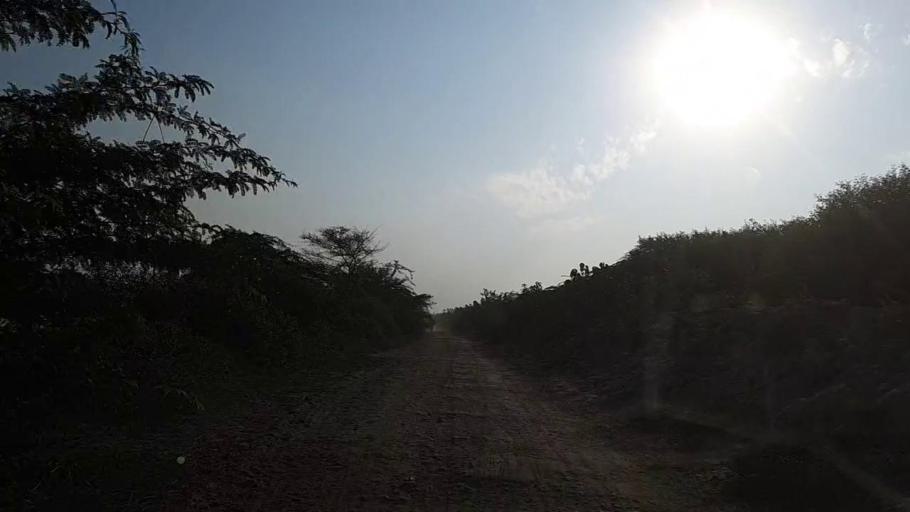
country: PK
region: Sindh
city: Mirpur Batoro
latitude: 24.7717
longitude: 68.2357
